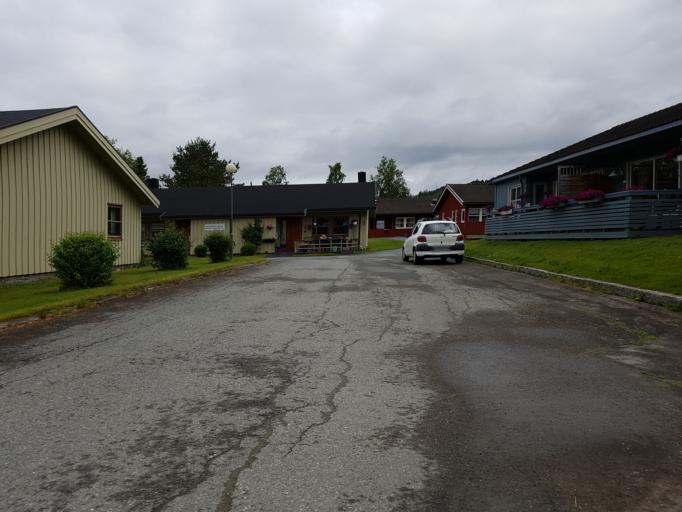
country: NO
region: Sor-Trondelag
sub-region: Selbu
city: Mebonden
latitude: 63.2177
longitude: 11.0367
